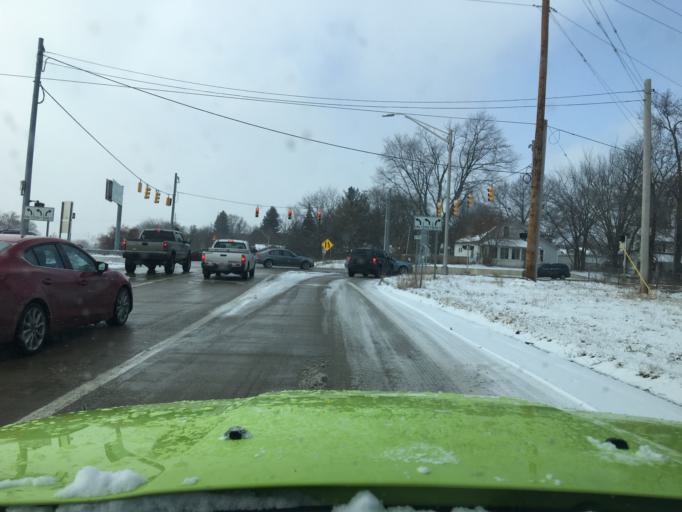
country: US
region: Michigan
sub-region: Kent County
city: Grand Rapids
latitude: 42.9742
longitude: -85.6392
